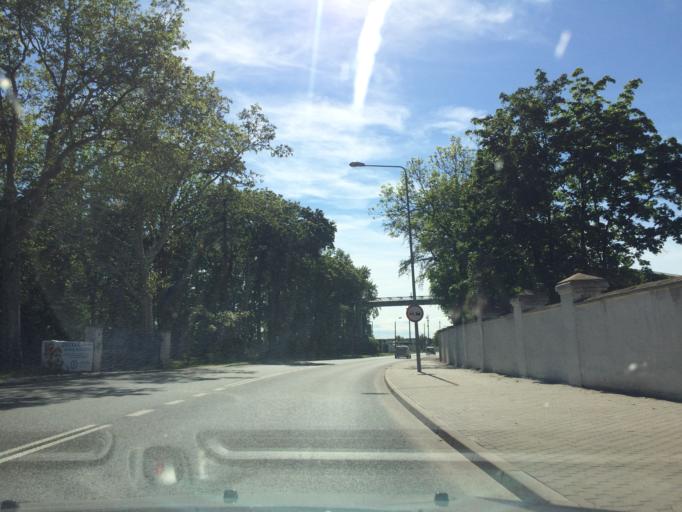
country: PL
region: Lower Silesian Voivodeship
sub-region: Powiat swidnicki
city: Swidnica
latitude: 50.8554
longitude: 16.5348
